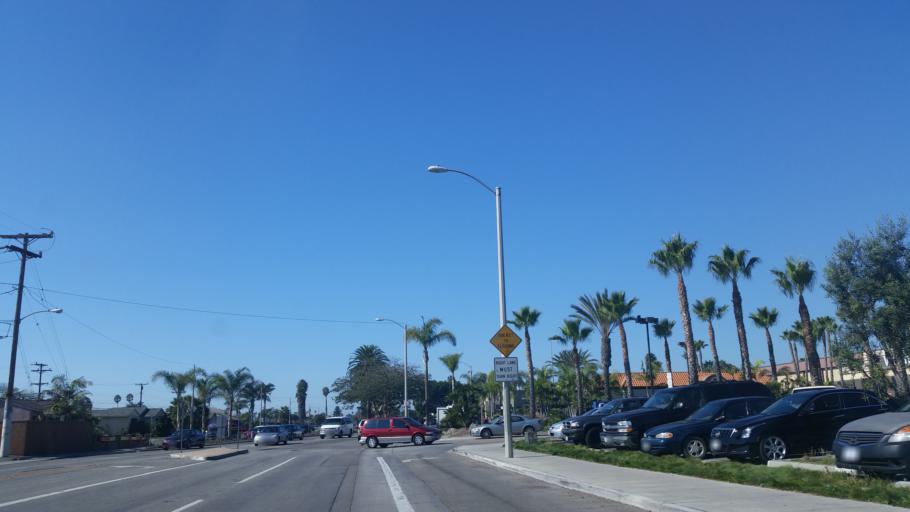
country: US
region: California
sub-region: Ventura County
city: Oxnard
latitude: 34.1735
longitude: -119.1783
